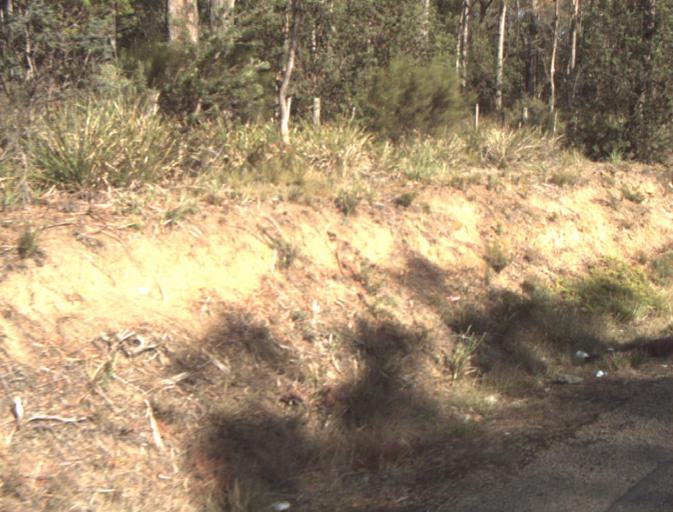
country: AU
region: Tasmania
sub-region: Launceston
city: Mayfield
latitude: -41.3195
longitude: 147.1896
